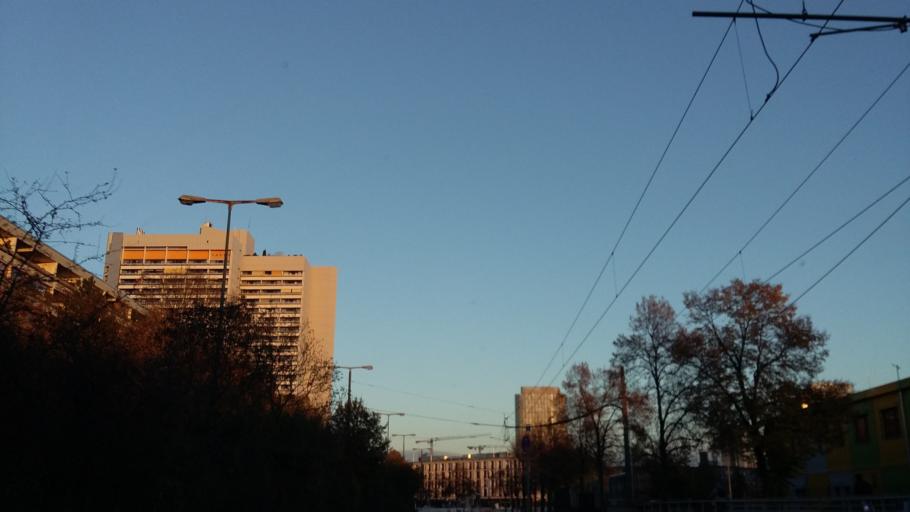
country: DE
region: Bavaria
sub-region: Upper Bavaria
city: Munich
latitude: 48.1348
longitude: 11.5197
